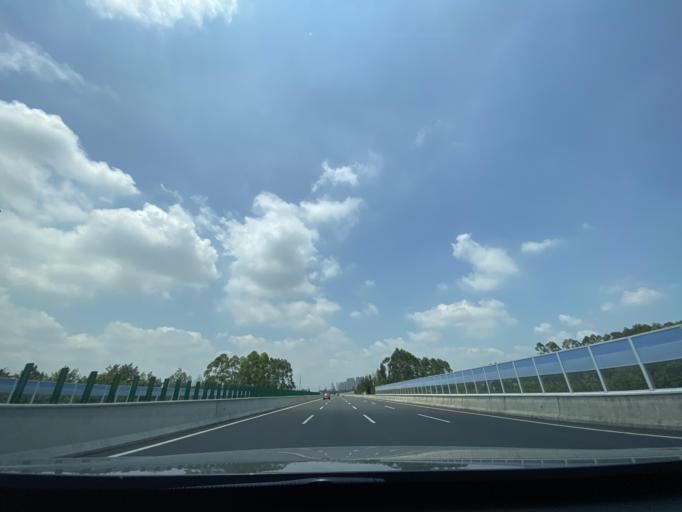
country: CN
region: Sichuan
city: Chengdu
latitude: 30.5781
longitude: 104.1344
